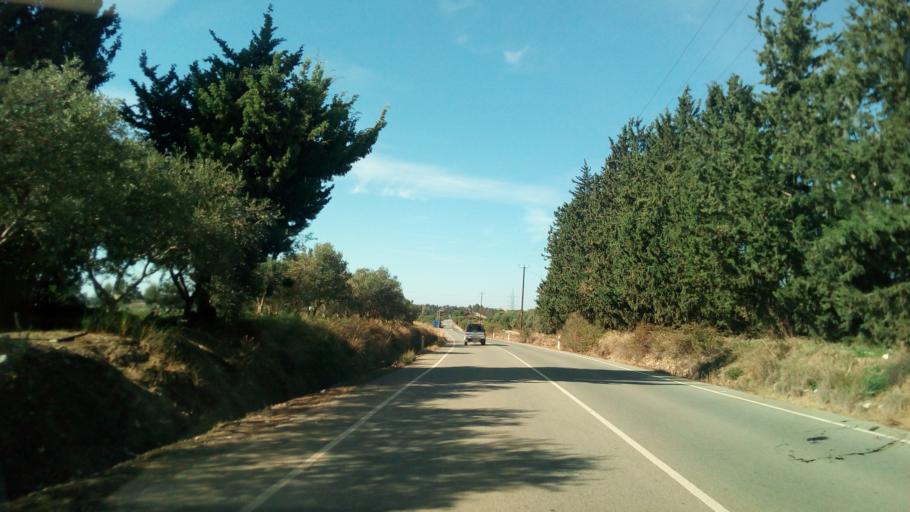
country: CY
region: Pafos
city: Mesogi
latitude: 34.7121
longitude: 32.5569
